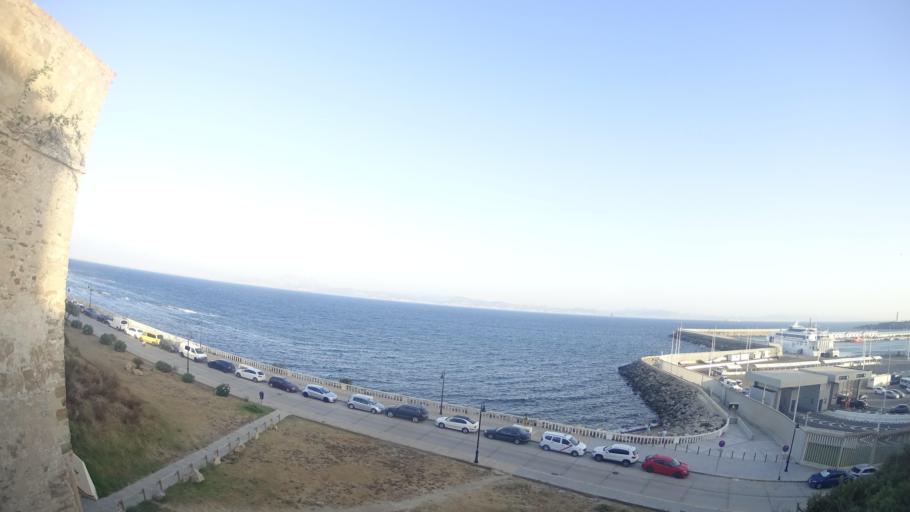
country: ES
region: Andalusia
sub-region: Provincia de Cadiz
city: Tarifa
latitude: 36.0120
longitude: -5.6011
